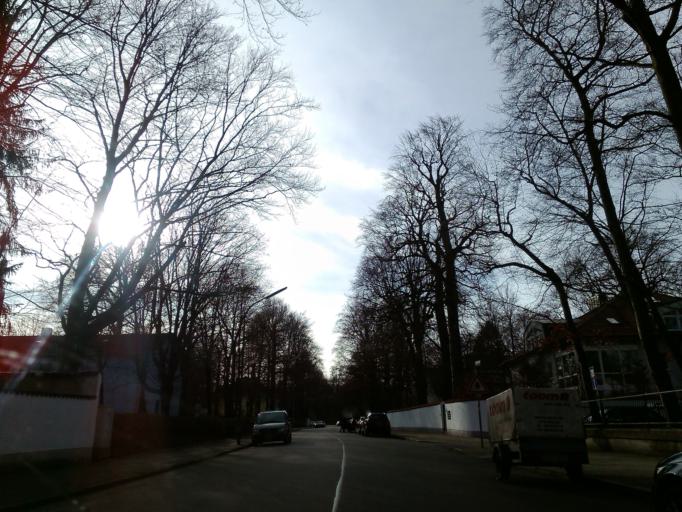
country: DE
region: Bavaria
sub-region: Upper Bavaria
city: Pullach im Isartal
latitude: 48.0869
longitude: 11.5500
